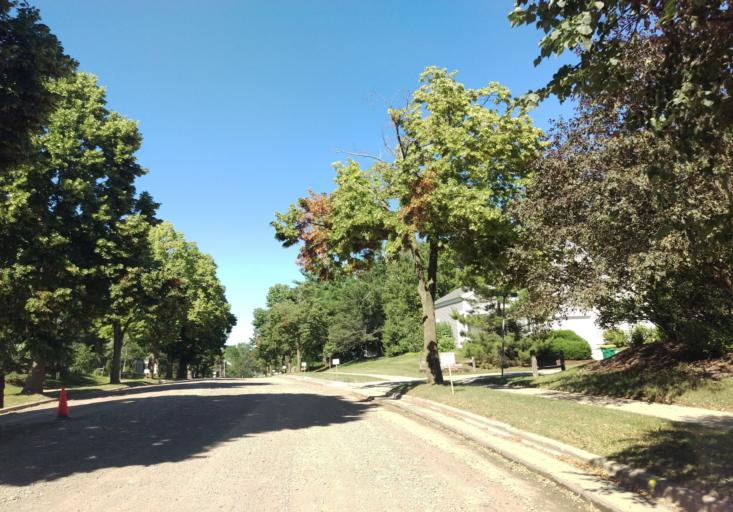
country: US
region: Wisconsin
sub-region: Dane County
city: Middleton
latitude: 43.0641
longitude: -89.5067
